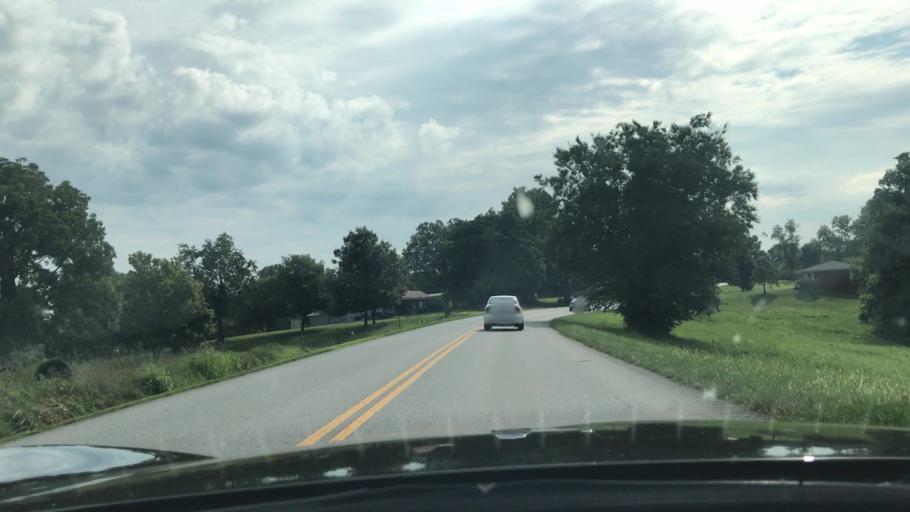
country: US
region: Kentucky
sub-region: Green County
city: Greensburg
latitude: 37.2689
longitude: -85.5369
